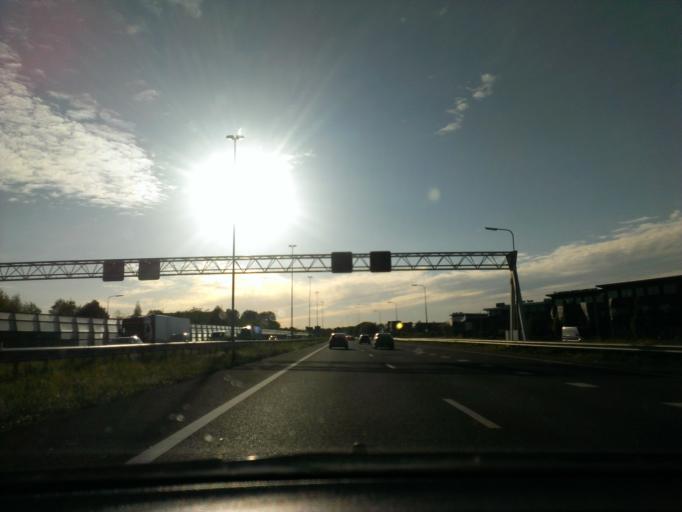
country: NL
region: South Holland
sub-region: Gemeente Sliedrecht
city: Sliedrecht
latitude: 51.8238
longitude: 4.8021
